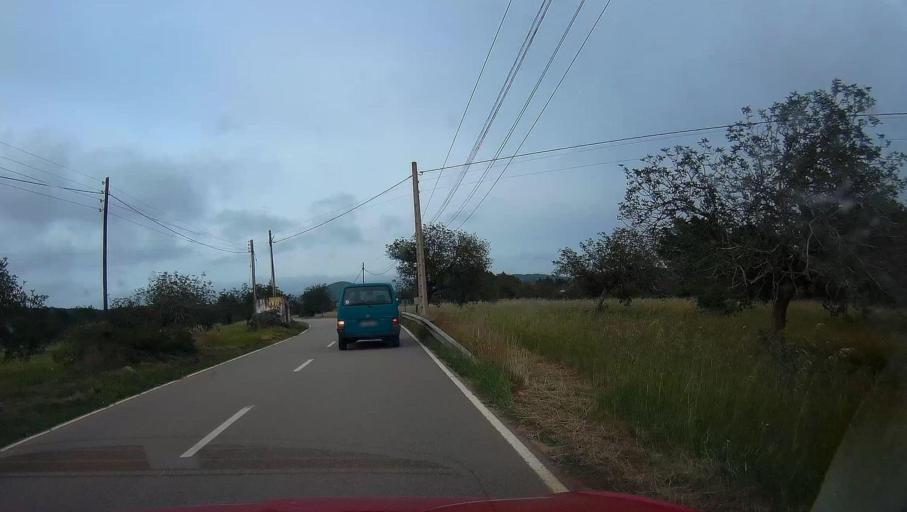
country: ES
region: Balearic Islands
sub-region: Illes Balears
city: Sant Joan de Labritja
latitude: 39.0463
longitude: 1.4149
